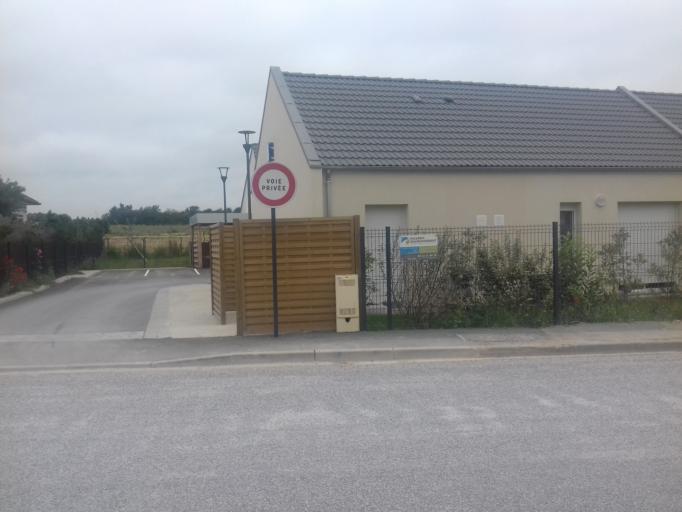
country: FR
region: Picardie
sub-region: Departement de la Somme
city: Pont-de-Metz
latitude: 49.8982
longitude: 2.2611
